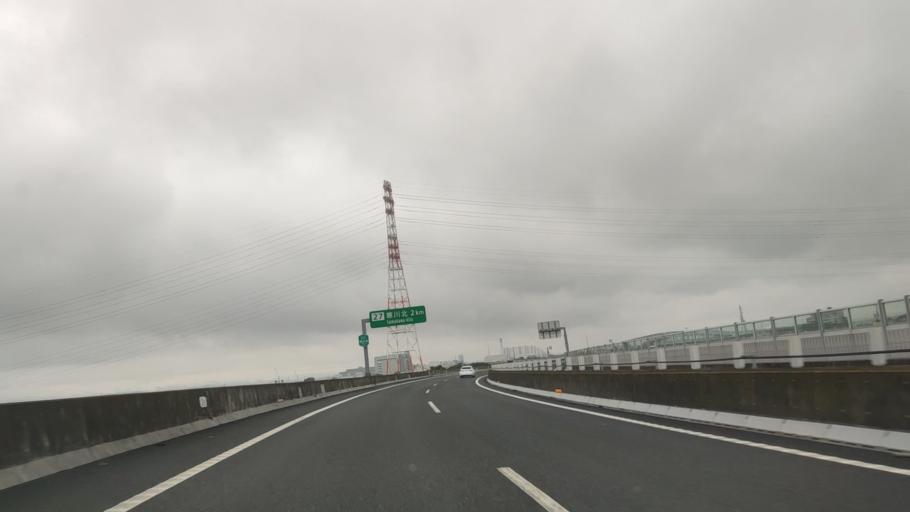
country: JP
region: Kanagawa
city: Chigasaki
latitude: 35.3655
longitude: 139.3731
